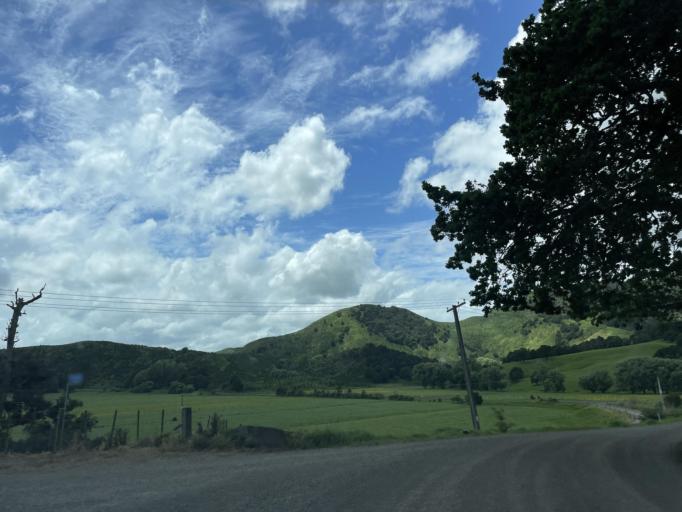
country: NZ
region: Northland
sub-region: Kaipara District
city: Dargaville
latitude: -35.8669
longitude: 174.0335
